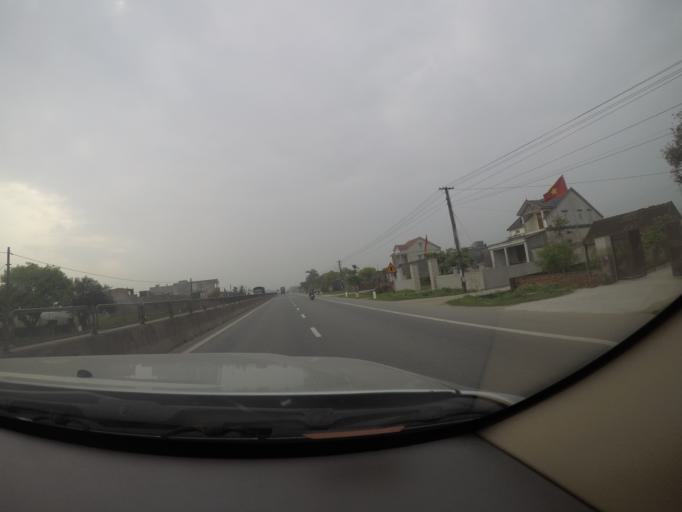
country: VN
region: Ha Tinh
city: Ky Anh
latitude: 18.1731
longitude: 106.2189
